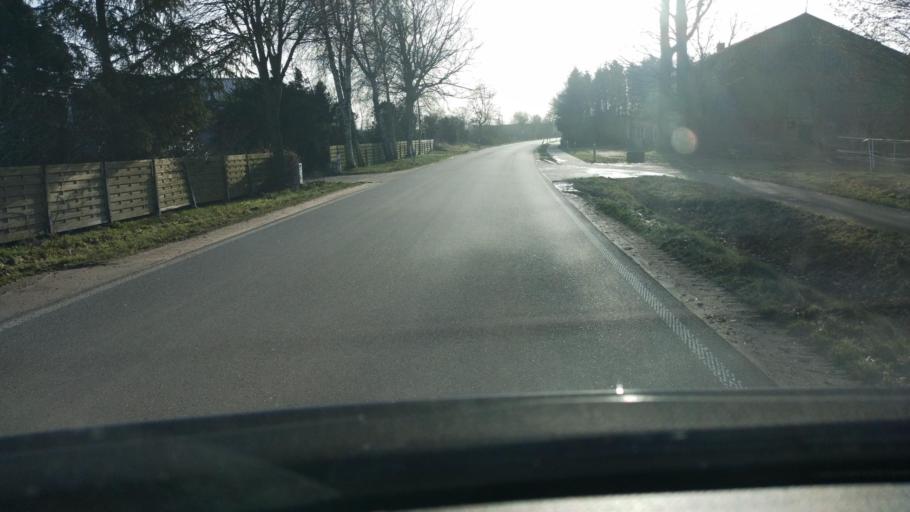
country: DE
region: Schleswig-Holstein
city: Jerrishoe
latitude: 54.6743
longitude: 9.3736
